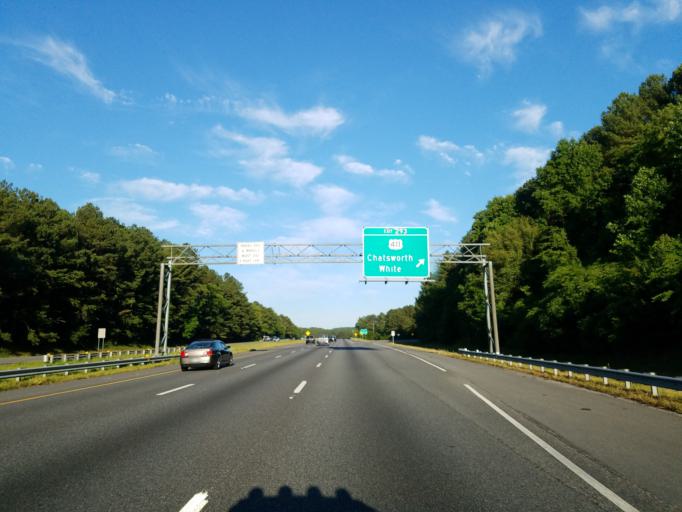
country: US
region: Georgia
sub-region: Bartow County
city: Cartersville
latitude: 34.2477
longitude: -84.7798
